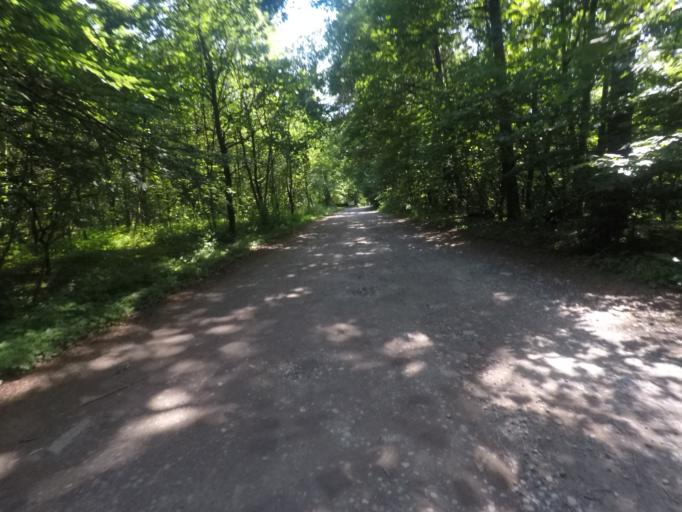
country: DE
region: North Rhine-Westphalia
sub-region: Regierungsbezirk Detmold
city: Bielefeld
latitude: 52.0033
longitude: 8.4831
